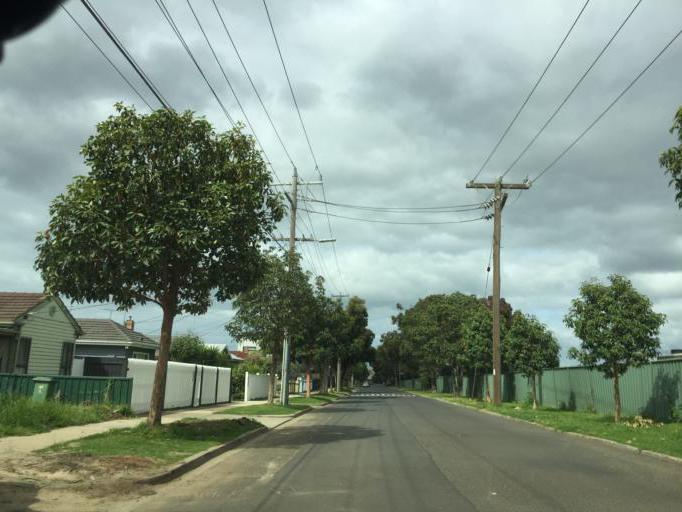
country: AU
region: Victoria
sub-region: Hobsons Bay
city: South Kingsville
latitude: -37.8150
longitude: 144.8626
